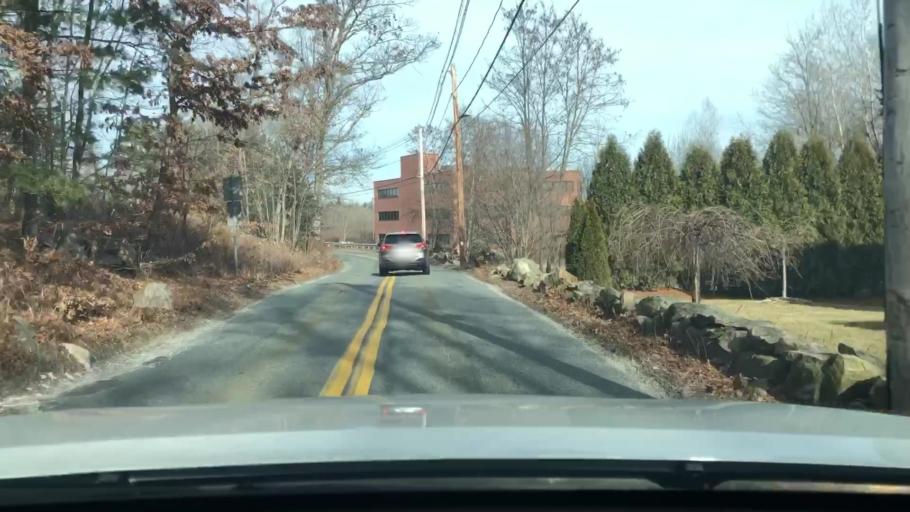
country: US
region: Massachusetts
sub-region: Worcester County
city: Milford
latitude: 42.1392
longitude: -71.4880
